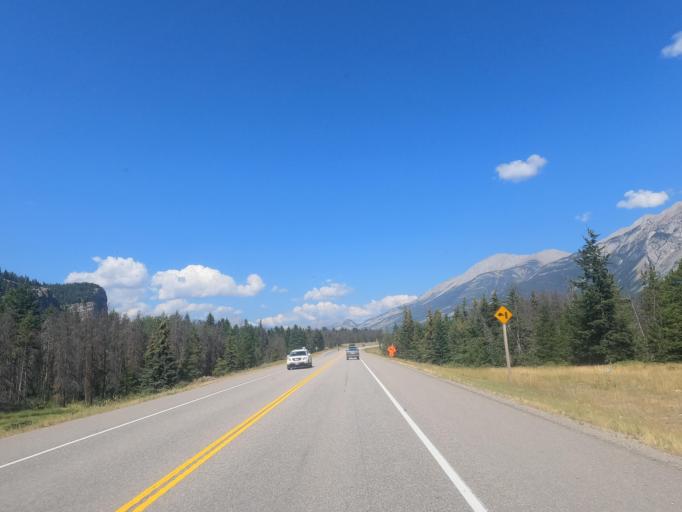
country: CA
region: Alberta
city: Jasper Park Lodge
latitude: 52.9366
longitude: -118.0388
